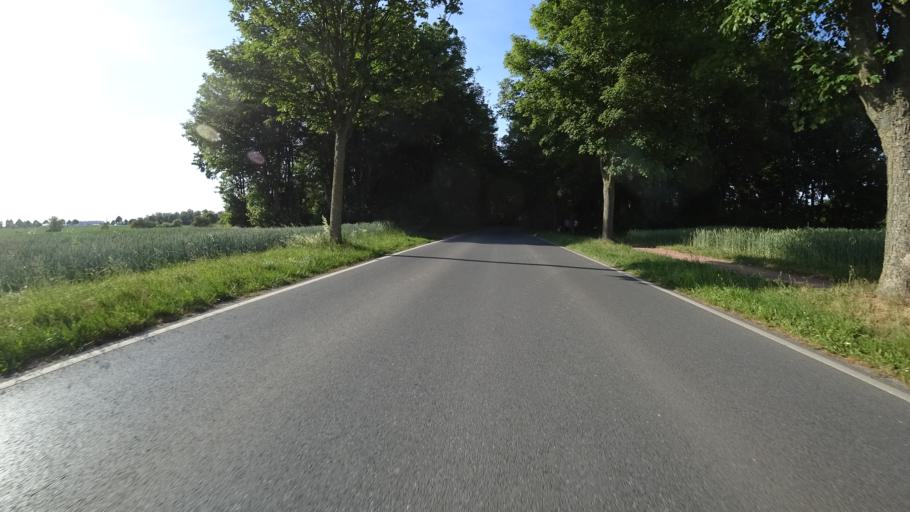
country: DE
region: North Rhine-Westphalia
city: Erwitte
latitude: 51.6298
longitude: 8.3502
